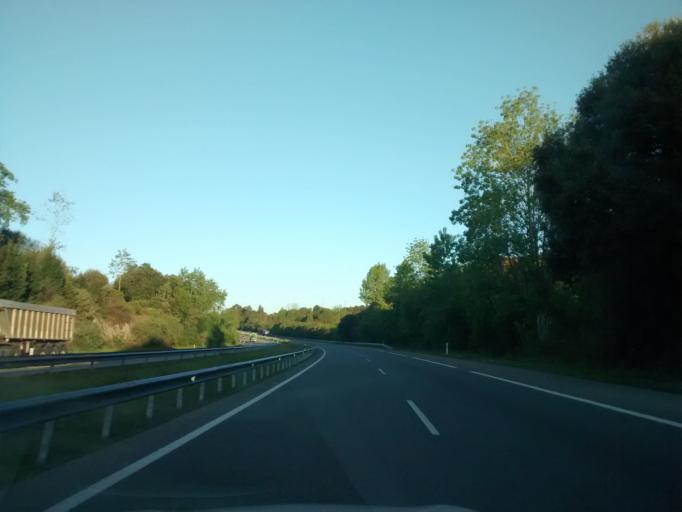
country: ES
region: Asturias
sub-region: Province of Asturias
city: Ribadesella
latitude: 43.4454
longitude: -4.9188
